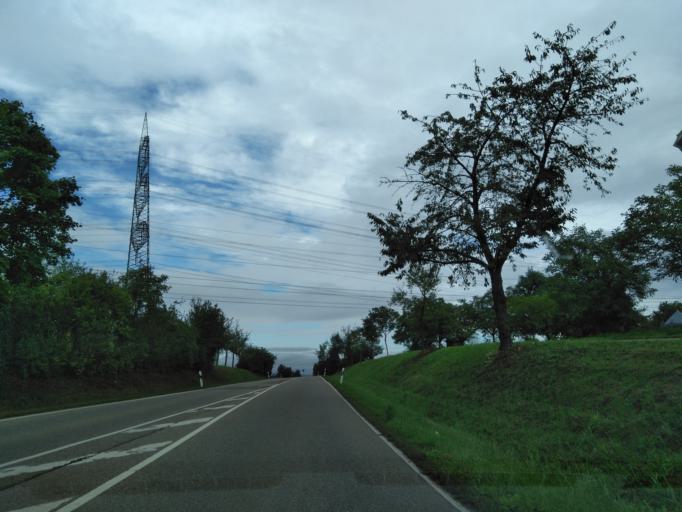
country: DE
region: Baden-Wuerttemberg
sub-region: Regierungsbezirk Stuttgart
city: Markgroningen
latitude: 48.9126
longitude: 9.0765
